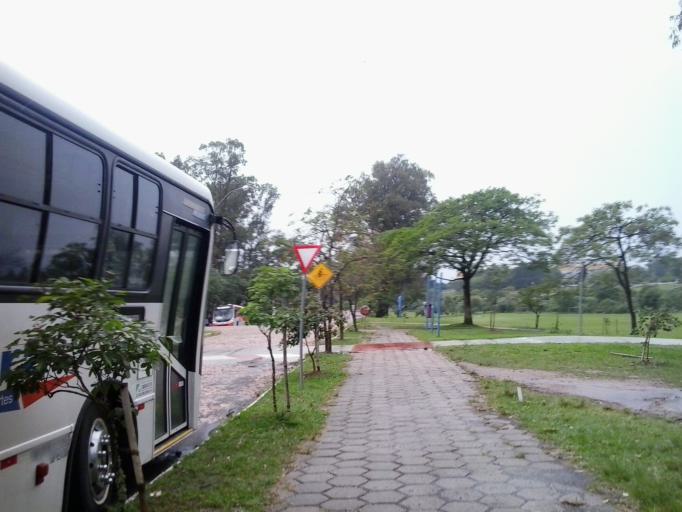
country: BR
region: Rio Grande do Sul
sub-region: Santa Maria
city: Santa Maria
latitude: -29.7193
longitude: -53.7156
